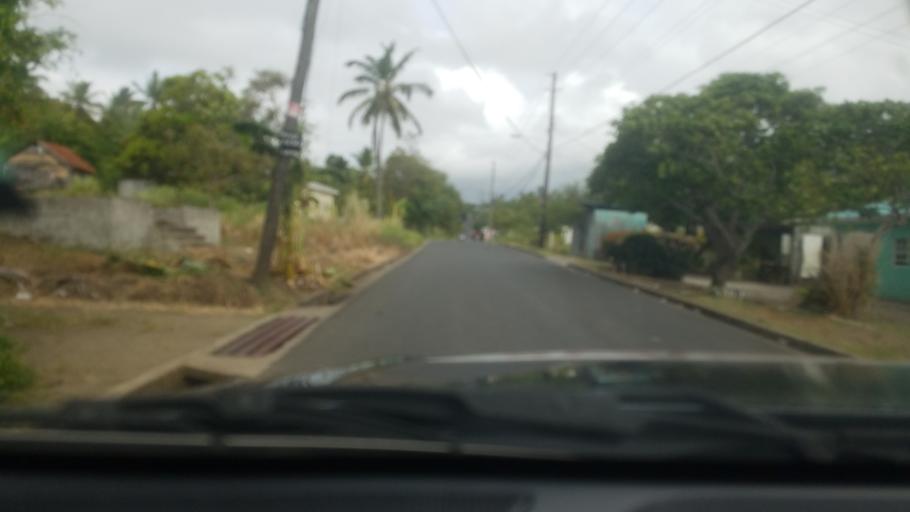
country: LC
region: Micoud Quarter
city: Micoud
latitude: 13.7973
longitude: -60.9157
